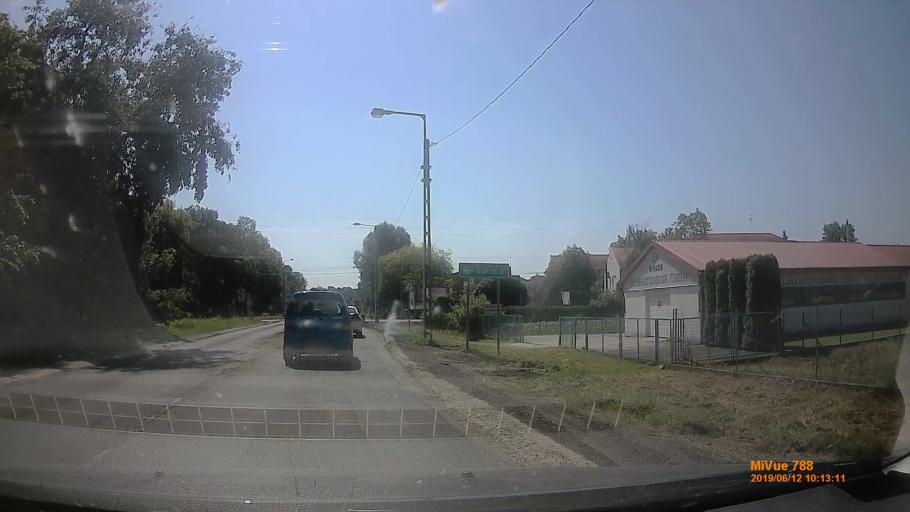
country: HU
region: Pest
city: Dabas
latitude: 47.2178
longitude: 19.2741
